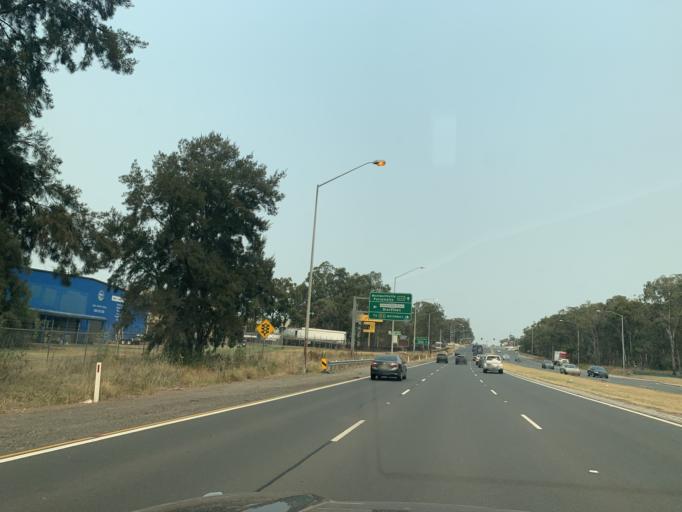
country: AU
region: New South Wales
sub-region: Blacktown
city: Blacktown
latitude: -33.7966
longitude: 150.8928
